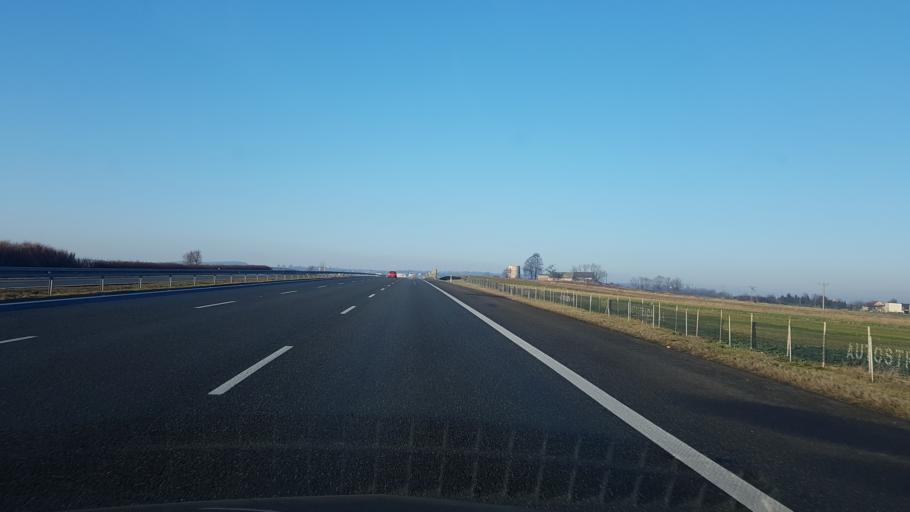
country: PL
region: Opole Voivodeship
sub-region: Powiat strzelecki
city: Lesnica
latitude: 50.4668
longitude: 18.2008
